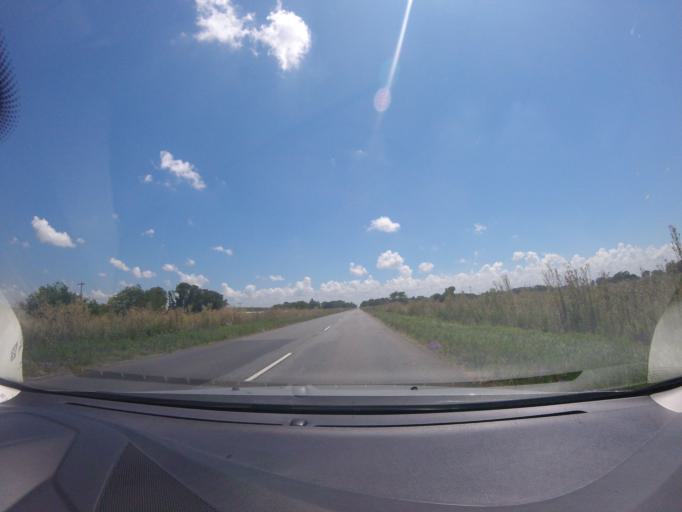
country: AR
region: Buenos Aires
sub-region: Partido de Las Flores
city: Las Flores
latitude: -36.2270
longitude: -59.0446
